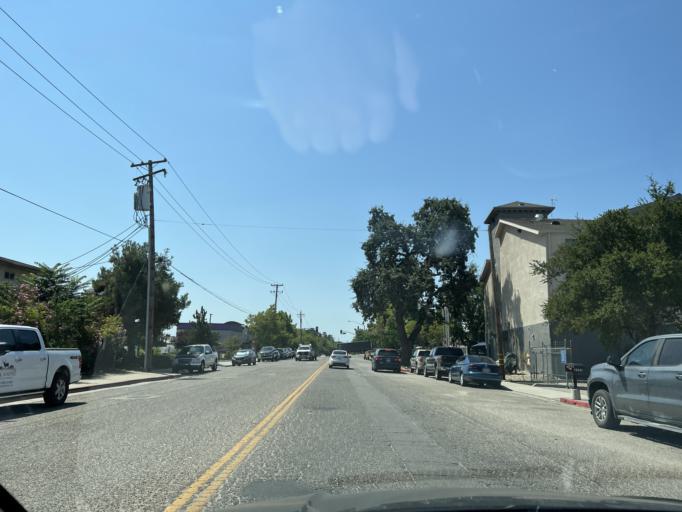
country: US
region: California
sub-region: San Luis Obispo County
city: Paso Robles
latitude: 35.6411
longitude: -120.6885
